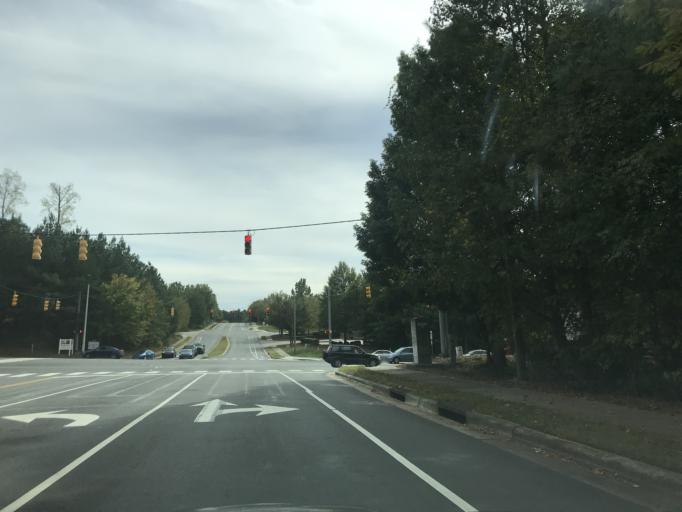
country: US
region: North Carolina
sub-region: Wake County
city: Wake Forest
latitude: 35.9463
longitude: -78.5451
